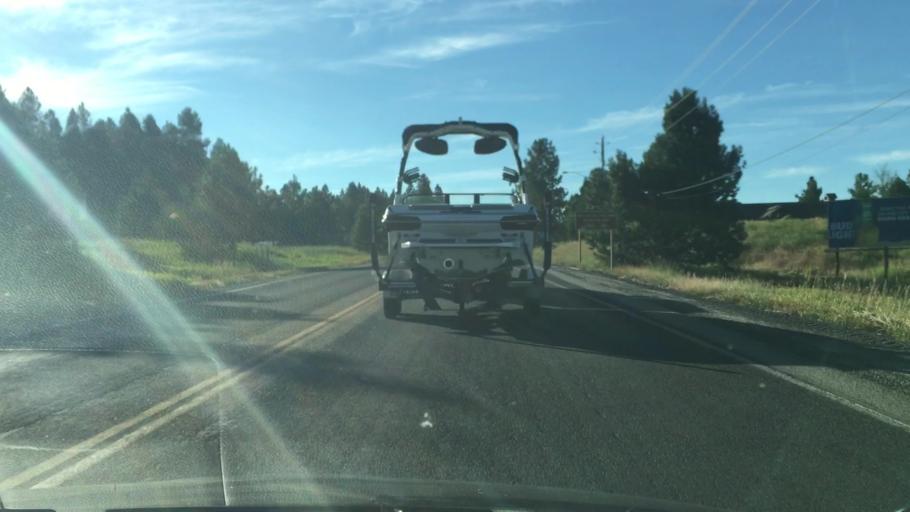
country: US
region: Idaho
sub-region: Valley County
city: Cascade
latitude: 44.5078
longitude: -116.0330
